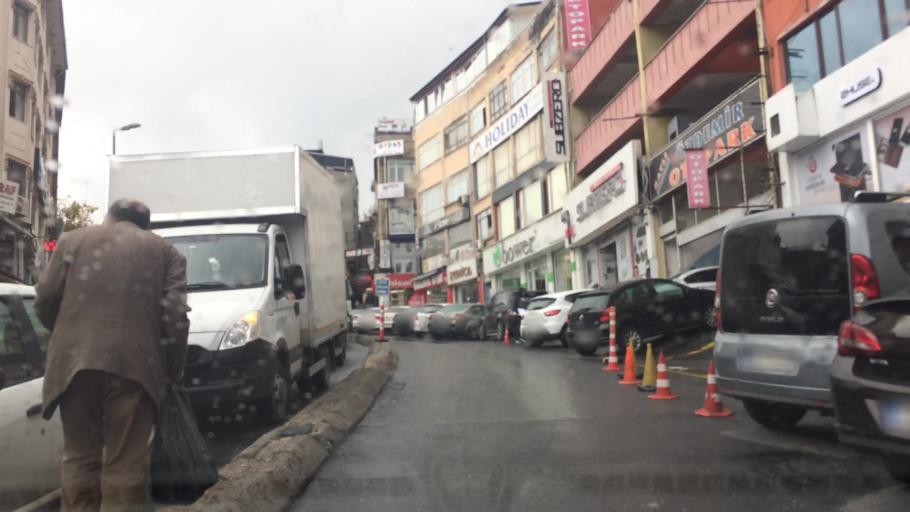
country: TR
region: Istanbul
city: Eminoenue
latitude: 41.0171
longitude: 28.9668
